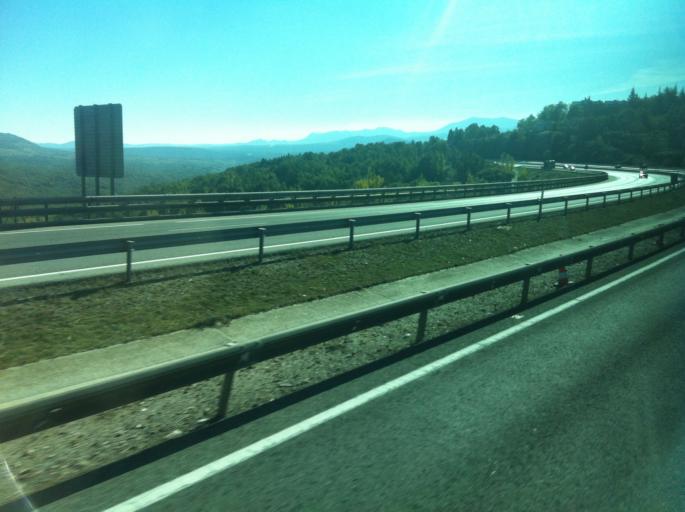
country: ES
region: Madrid
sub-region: Provincia de Madrid
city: Robregordo
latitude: 41.1061
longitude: -3.5909
